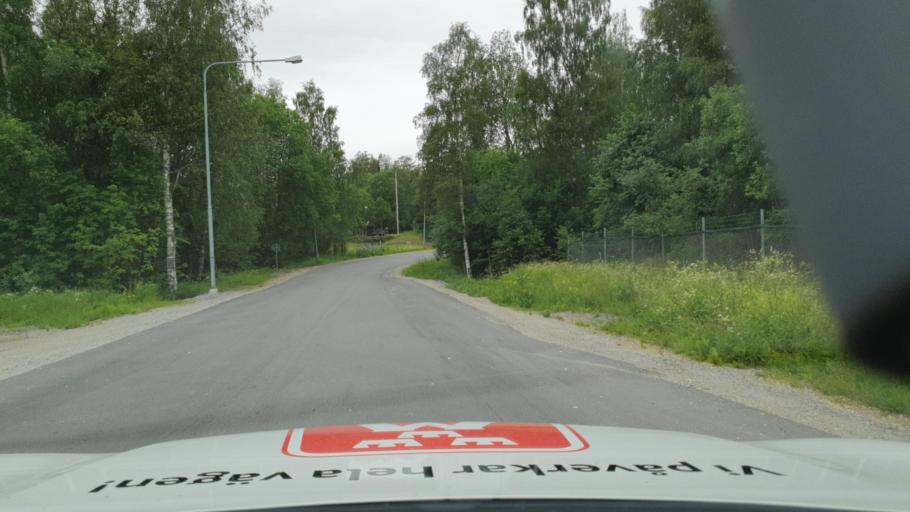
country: SE
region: Vaesterbotten
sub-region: Nordmalings Kommun
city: Nordmaling
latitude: 63.5348
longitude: 19.4456
